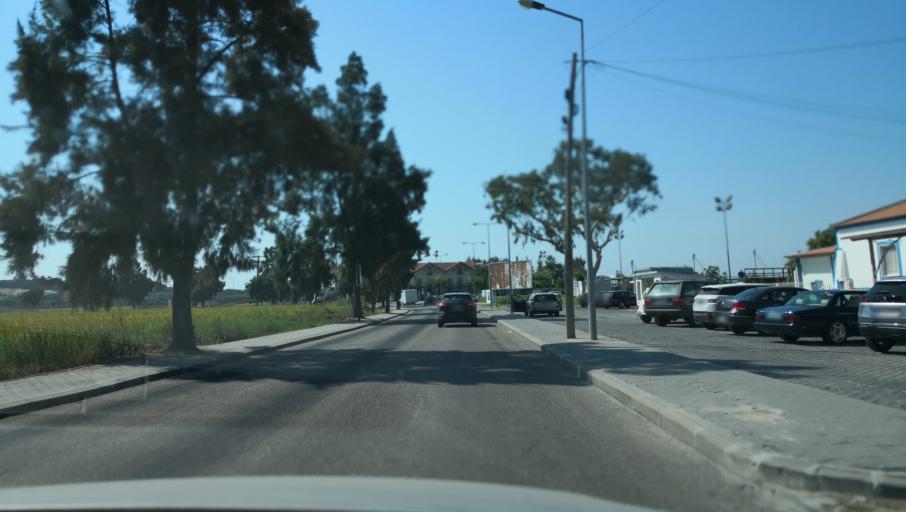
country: PT
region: Setubal
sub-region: Alcacer do Sal
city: Alcacer do Sal
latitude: 38.3697
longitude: -8.5089
